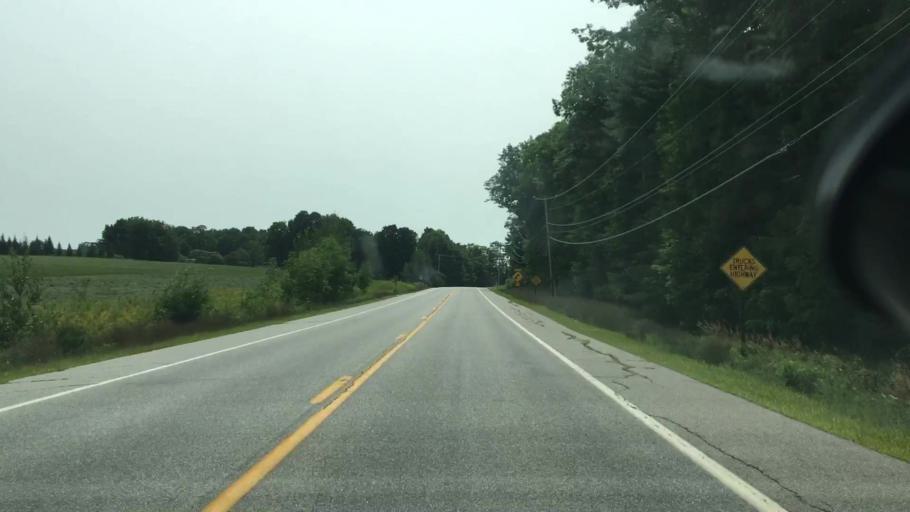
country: US
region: Maine
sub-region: Androscoggin County
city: Livermore Falls
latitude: 44.4254
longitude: -70.1450
